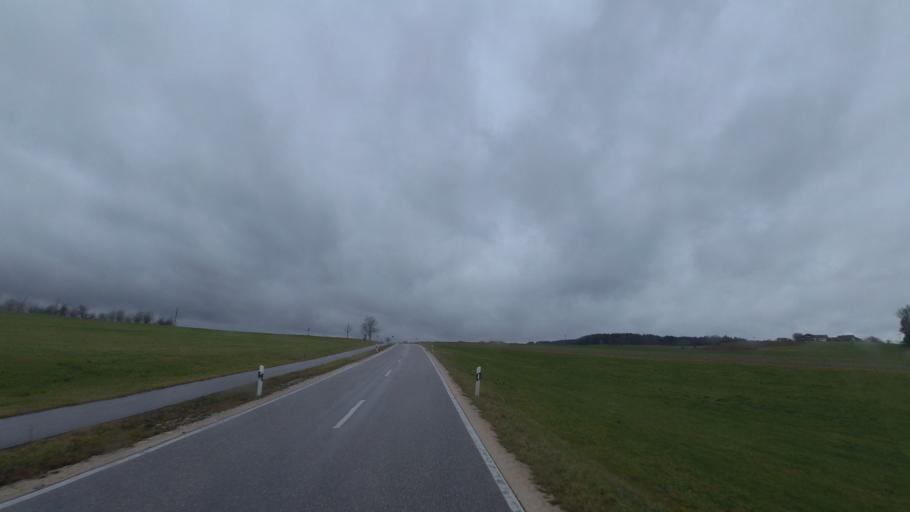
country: DE
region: Bavaria
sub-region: Upper Bavaria
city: Taching am See
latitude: 47.9557
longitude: 12.7772
